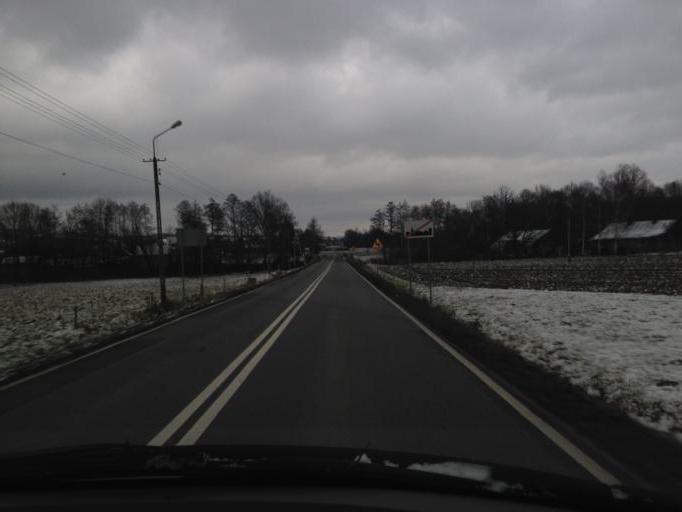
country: PL
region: Lesser Poland Voivodeship
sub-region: Powiat tarnowski
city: Janowice
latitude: 49.8553
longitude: 20.8659
